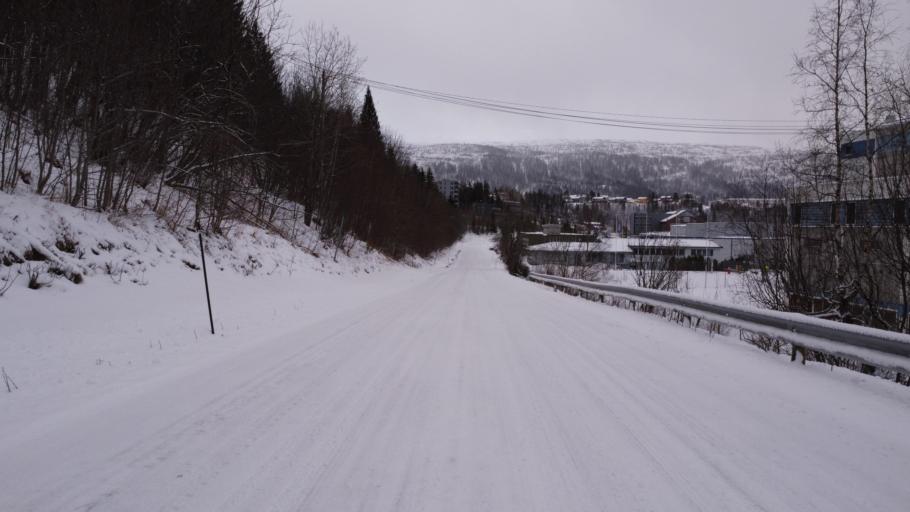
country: NO
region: Nordland
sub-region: Rana
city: Mo i Rana
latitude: 66.3234
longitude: 14.1543
